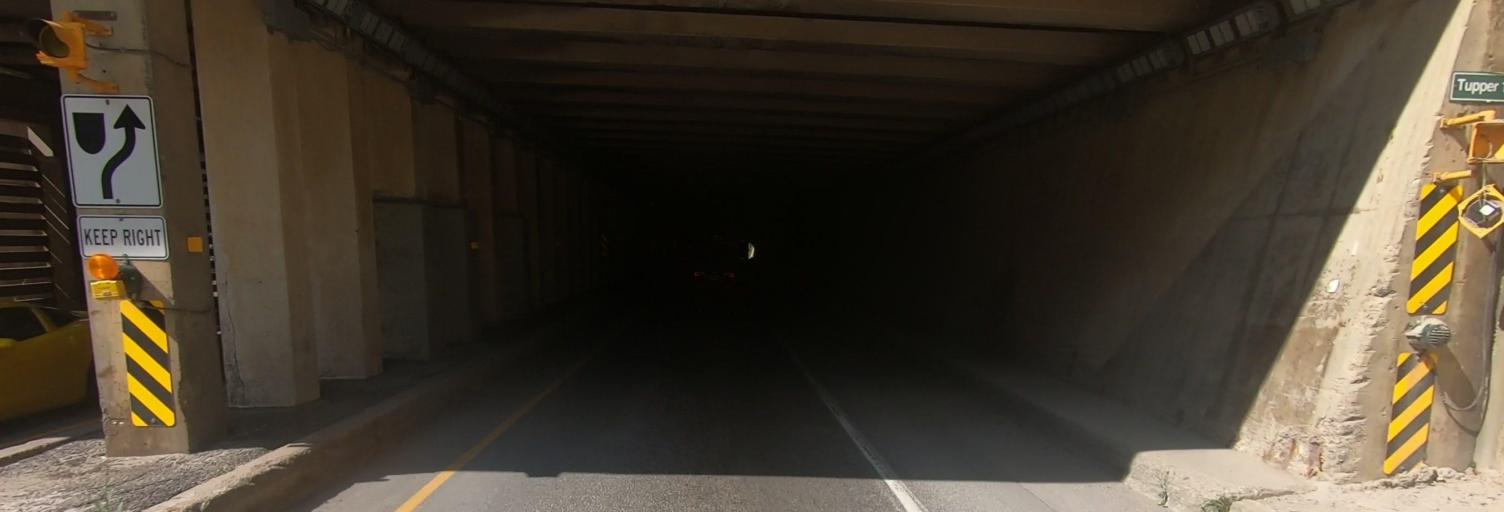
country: CA
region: British Columbia
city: Golden
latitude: 51.3285
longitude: -117.4677
